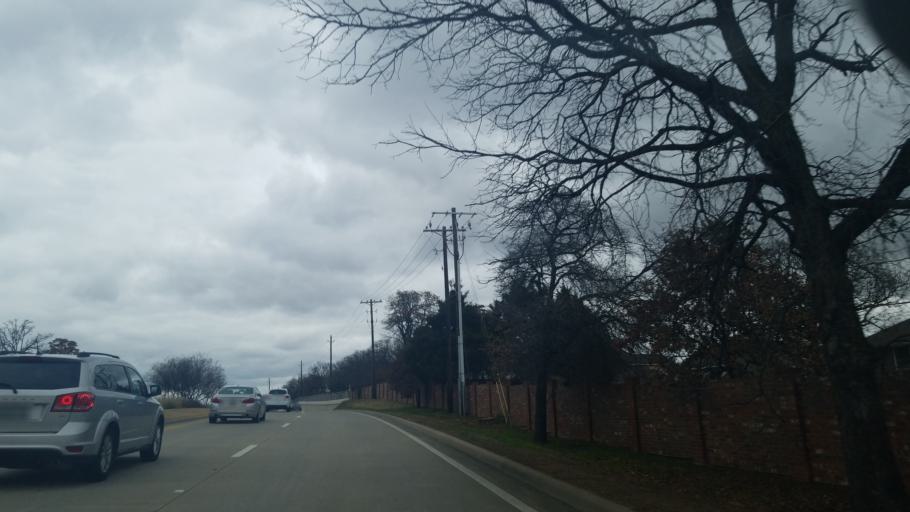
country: US
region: Texas
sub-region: Denton County
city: Copper Canyon
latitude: 33.0887
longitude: -97.0783
